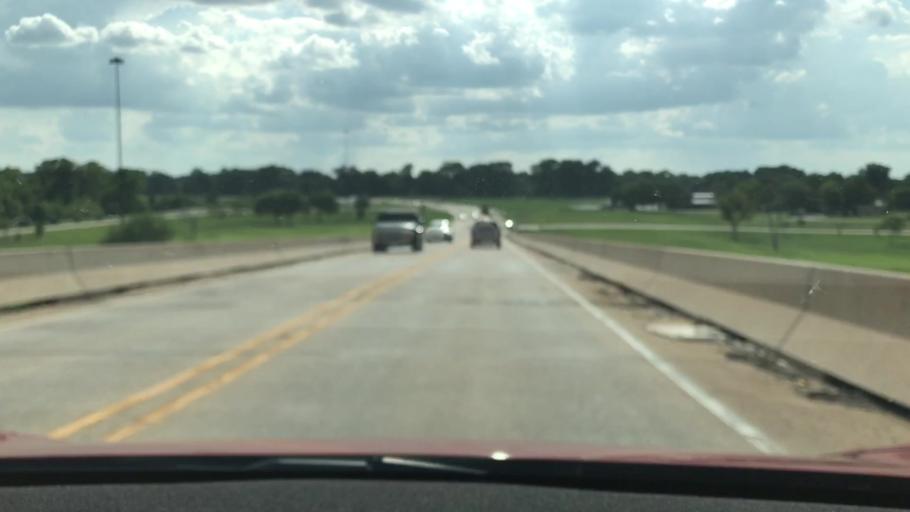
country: US
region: Louisiana
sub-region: Bossier Parish
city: Bossier City
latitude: 32.4588
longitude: -93.6824
